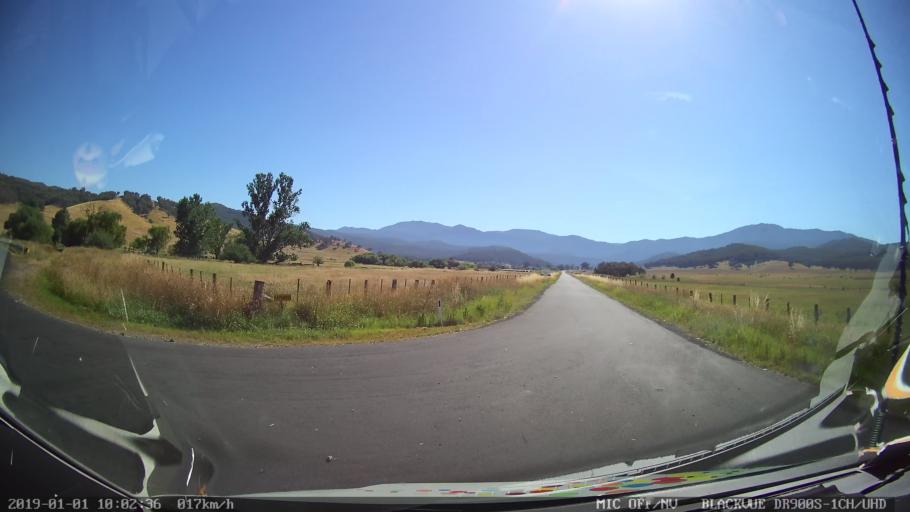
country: AU
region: New South Wales
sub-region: Snowy River
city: Jindabyne
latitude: -36.1809
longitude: 148.1022
